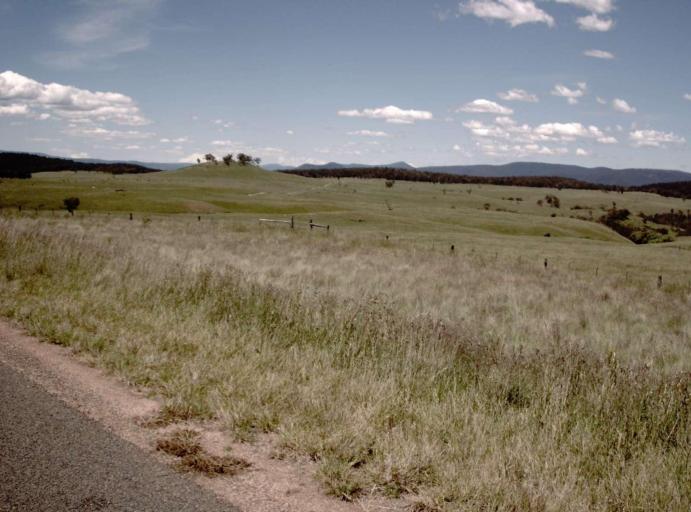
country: AU
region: New South Wales
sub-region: Snowy River
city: Jindabyne
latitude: -37.0942
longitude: 148.2650
